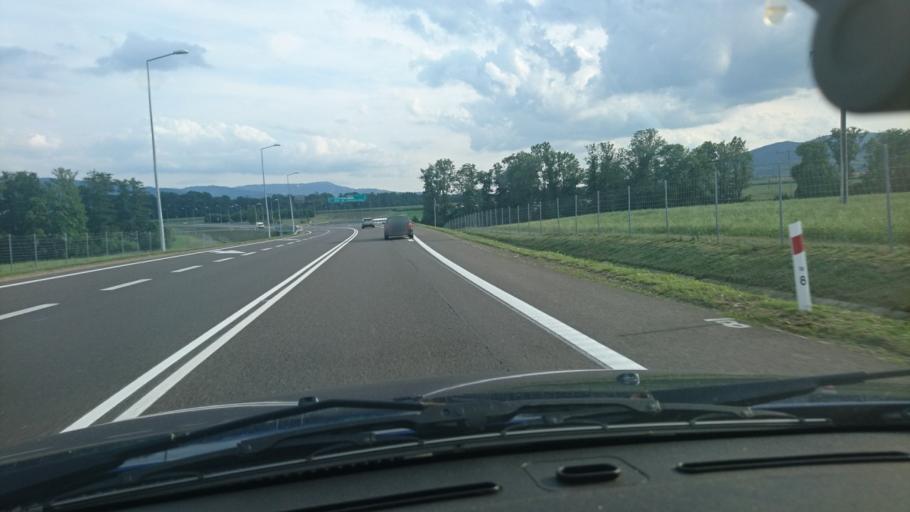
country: PL
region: Silesian Voivodeship
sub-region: Powiat zywiecki
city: Wieprz
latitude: 49.6617
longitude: 19.1667
